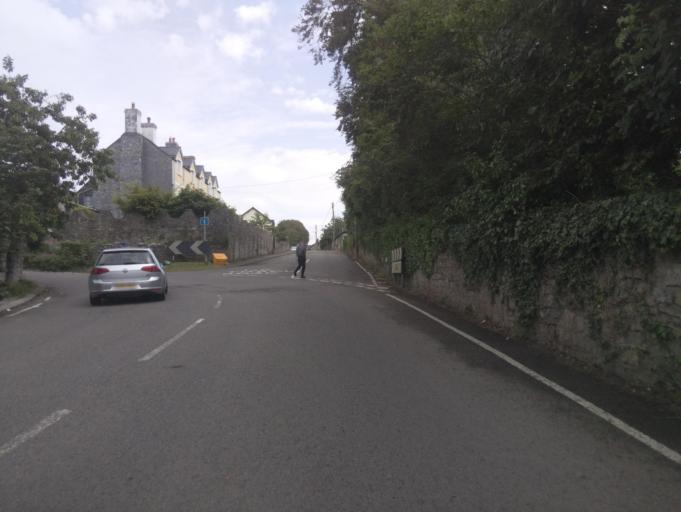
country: GB
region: Wales
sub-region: Vale of Glamorgan
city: Llantwit Major
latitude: 51.4059
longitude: -3.4634
